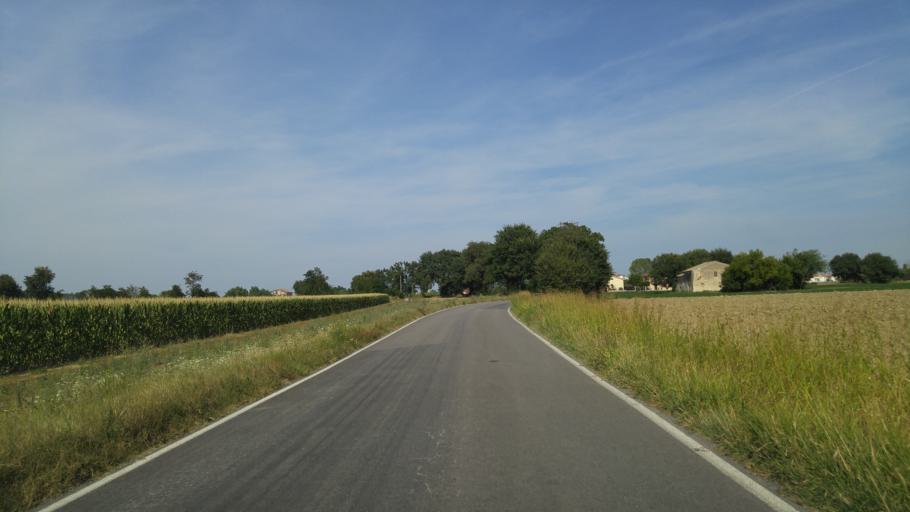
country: IT
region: The Marches
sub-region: Provincia di Pesaro e Urbino
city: Cuccurano
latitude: 43.7947
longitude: 12.9820
